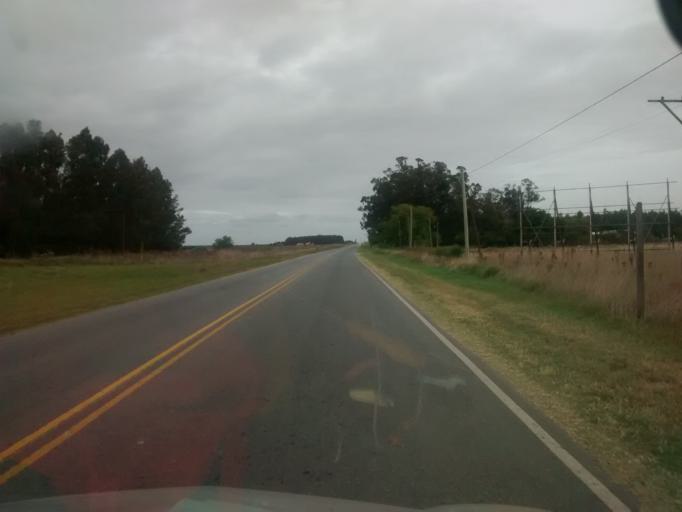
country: AR
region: Buenos Aires
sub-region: Partido de Loberia
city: Loberia
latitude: -38.2062
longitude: -58.7352
